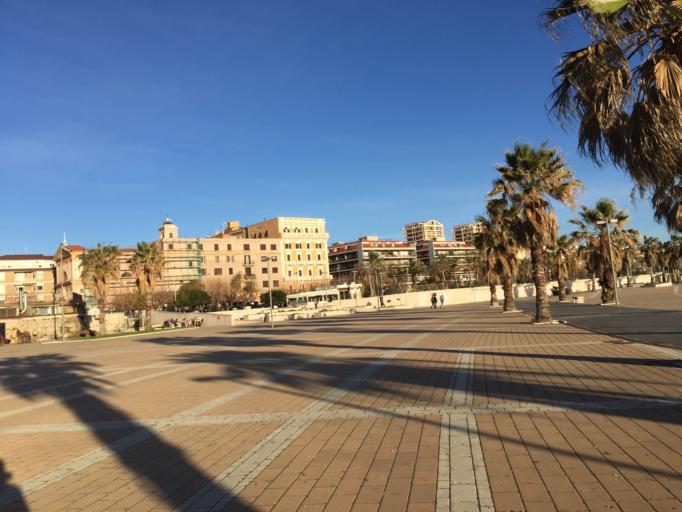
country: IT
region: Latium
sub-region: Citta metropolitana di Roma Capitale
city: Civitavecchia
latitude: 42.0895
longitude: 11.7918
